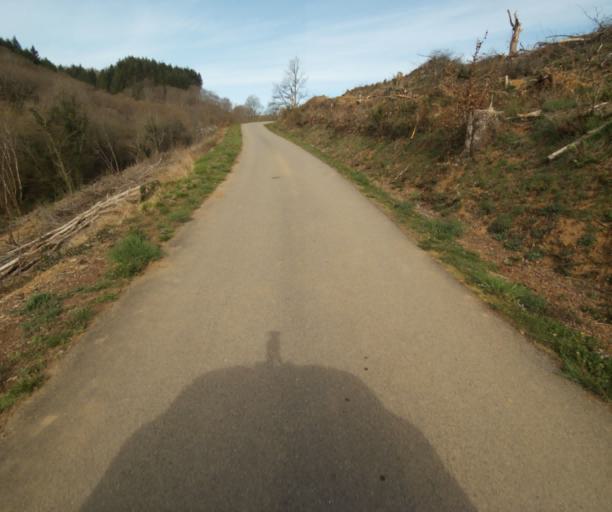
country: FR
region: Limousin
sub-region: Departement de la Correze
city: Seilhac
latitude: 45.4151
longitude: 1.7935
